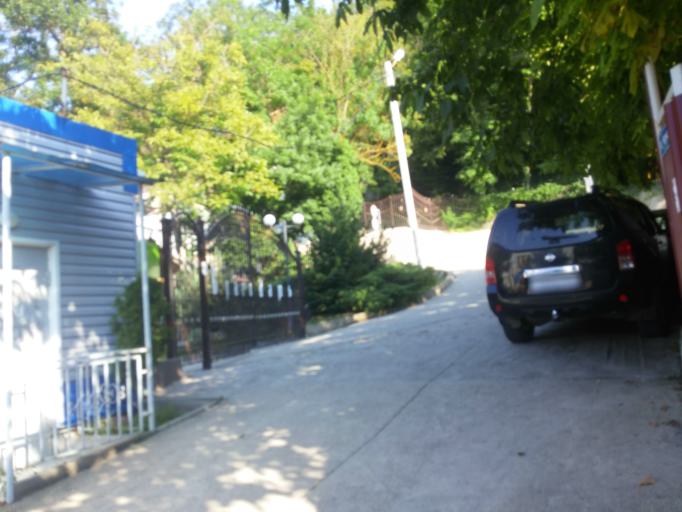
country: RU
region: Krasnodarskiy
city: Divnomorskoye
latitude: 44.4645
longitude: 38.1577
